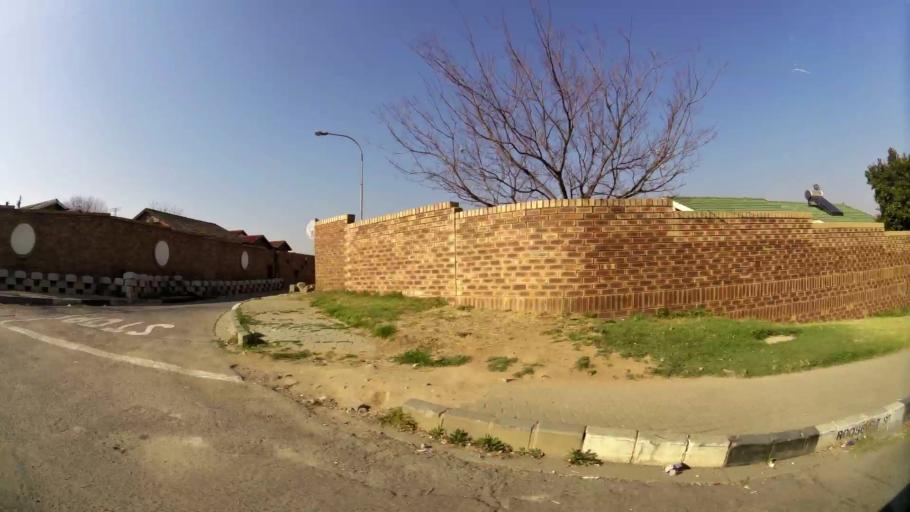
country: ZA
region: Gauteng
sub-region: City of Johannesburg Metropolitan Municipality
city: Modderfontein
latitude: -26.1044
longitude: 28.1114
